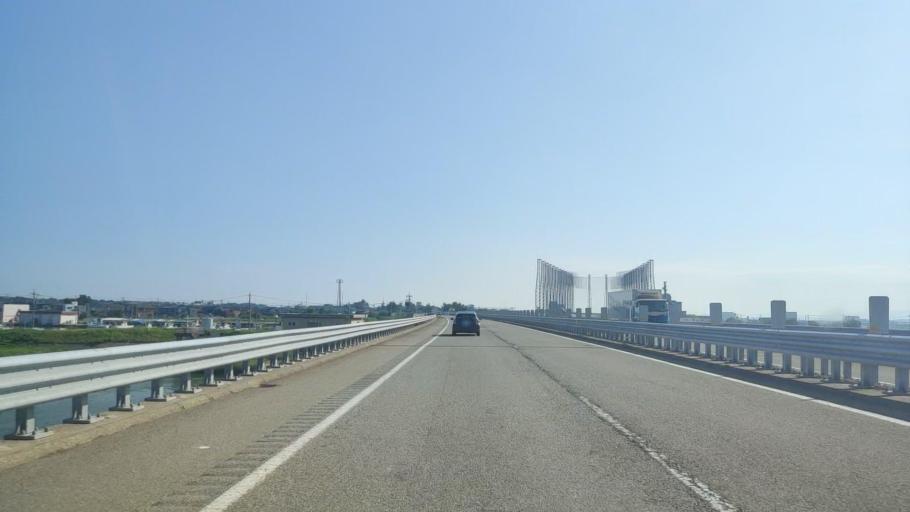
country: JP
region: Ishikawa
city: Komatsu
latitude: 36.4157
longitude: 136.4258
